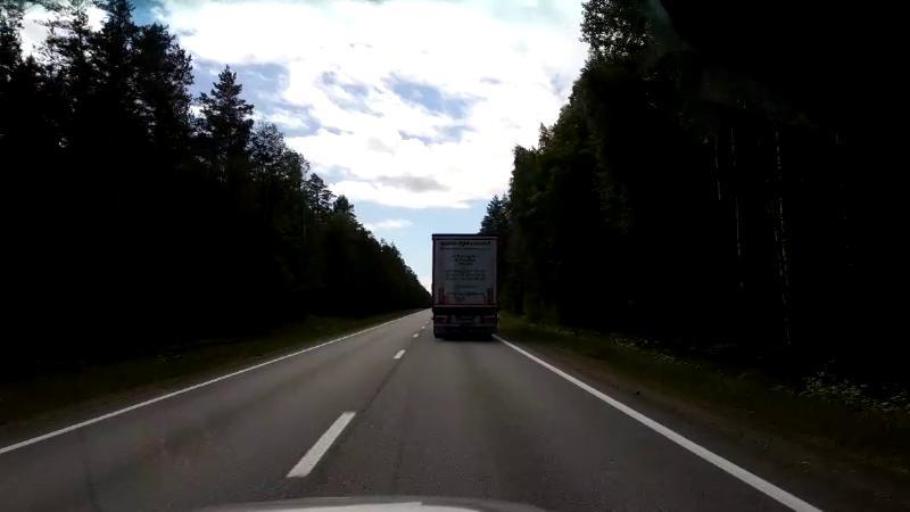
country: LV
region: Salacgrivas
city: Salacgriva
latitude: 57.5222
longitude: 24.4308
